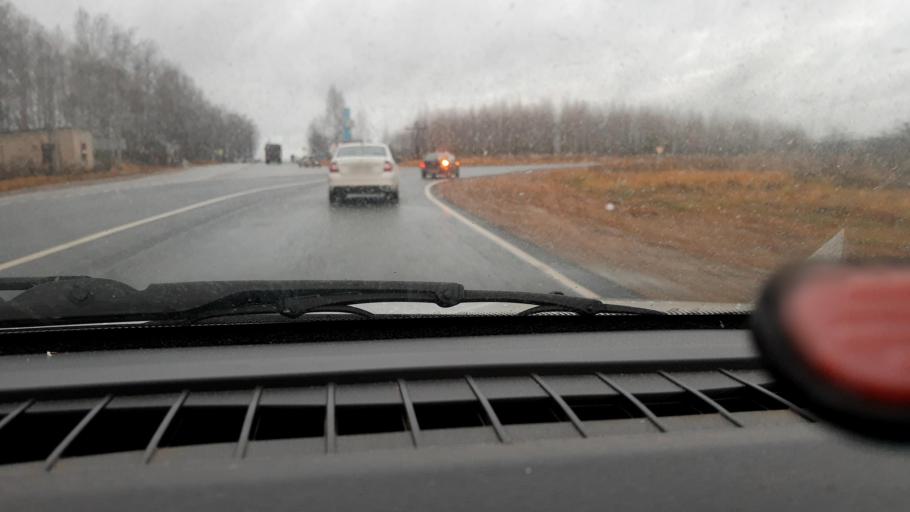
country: RU
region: Nizjnij Novgorod
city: Krasnyye Baki
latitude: 57.0942
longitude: 45.1503
